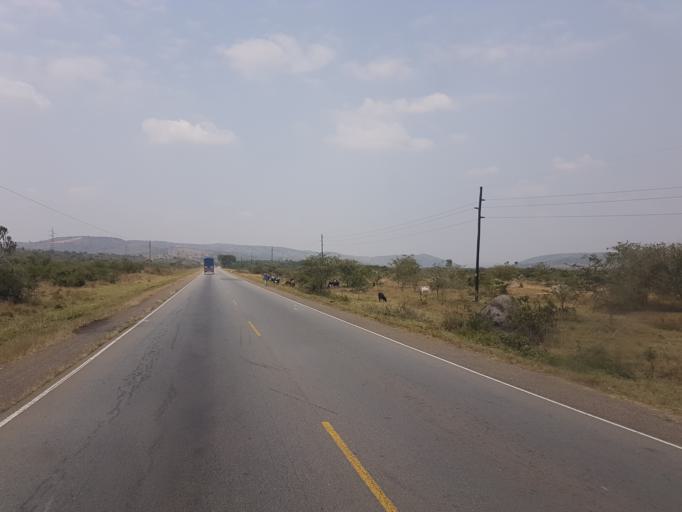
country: UG
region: Western Region
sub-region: Mbarara District
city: Mbarara
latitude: -0.5102
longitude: 30.8280
